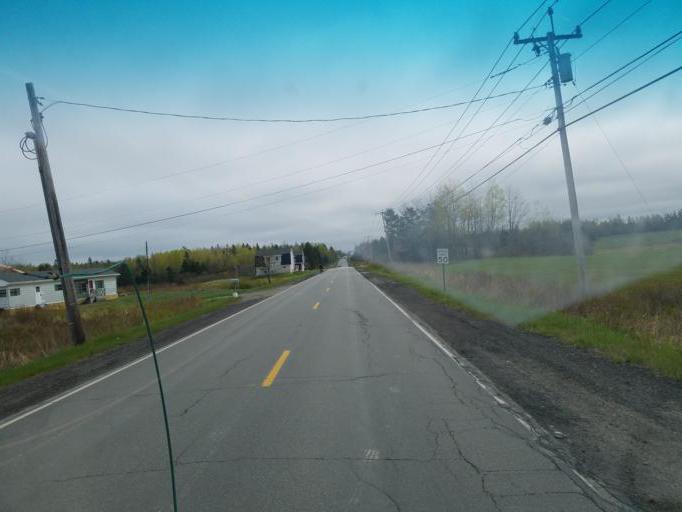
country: US
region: Maine
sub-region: Washington County
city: Eastport
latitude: 44.8359
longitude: -67.0249
